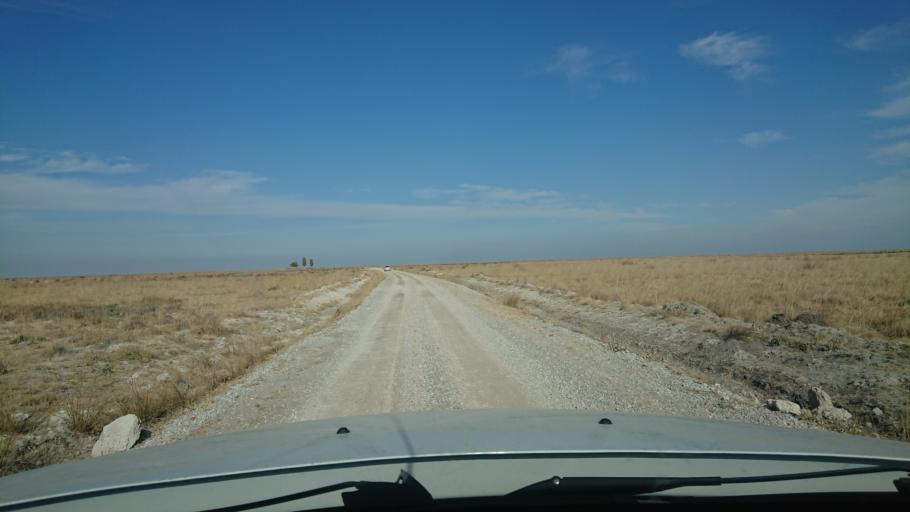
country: TR
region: Aksaray
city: Eskil
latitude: 38.4677
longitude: 33.4552
